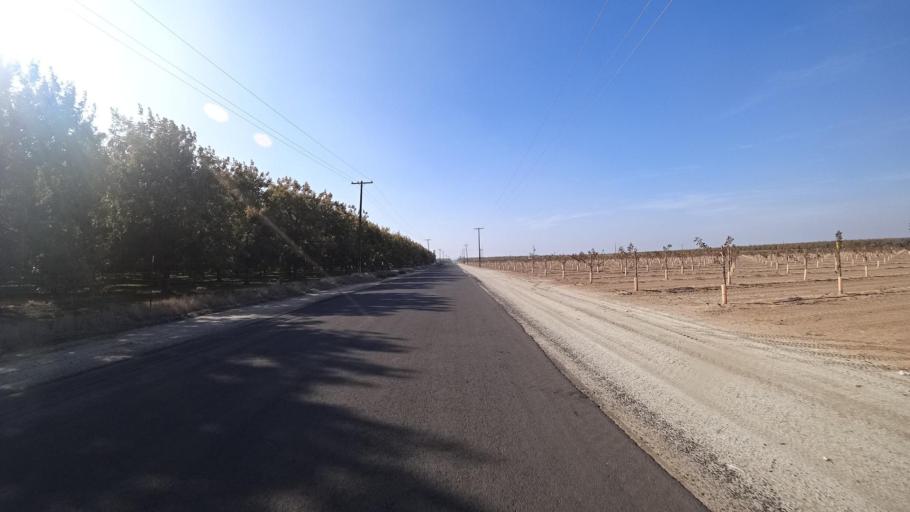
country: US
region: California
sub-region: Kern County
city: McFarland
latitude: 35.6311
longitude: -119.1926
